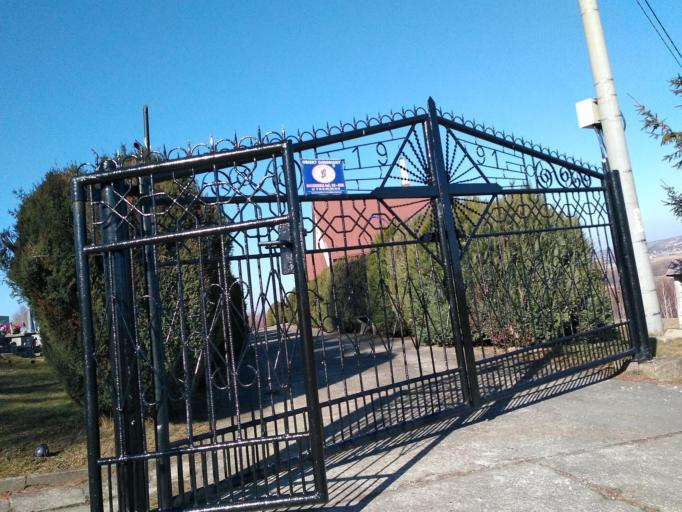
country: PL
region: Subcarpathian Voivodeship
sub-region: Powiat rzeszowski
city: Siedliska
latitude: 49.9459
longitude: 21.9526
